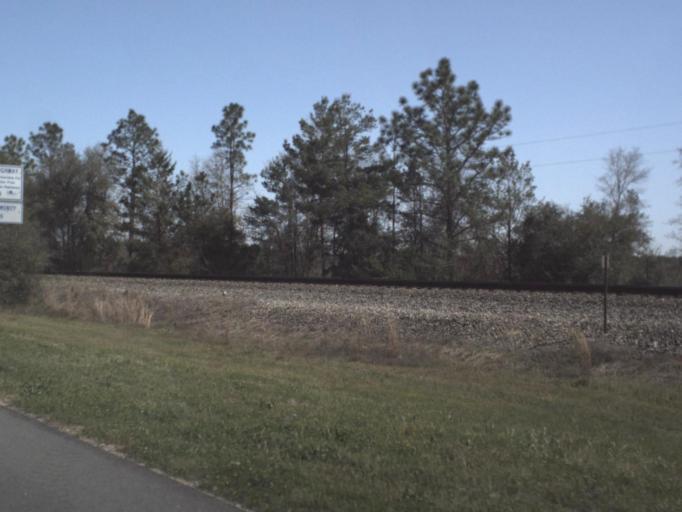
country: US
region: Florida
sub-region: Okaloosa County
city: Crestview
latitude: 30.7427
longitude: -86.3917
